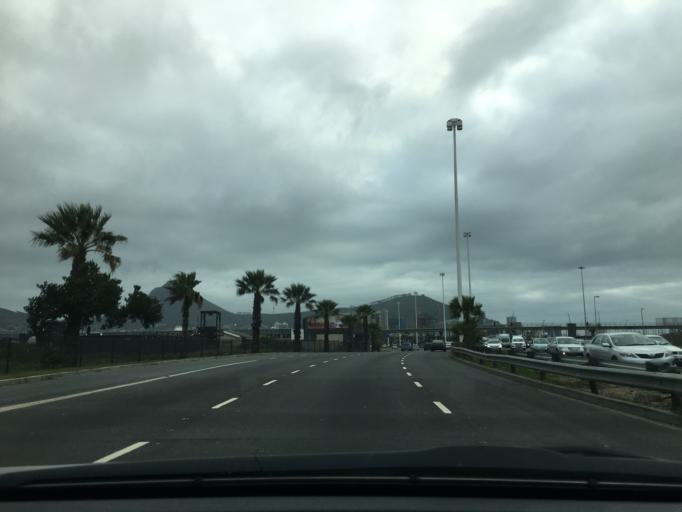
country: ZA
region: Western Cape
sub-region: City of Cape Town
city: Cape Town
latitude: -33.9216
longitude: 18.4482
